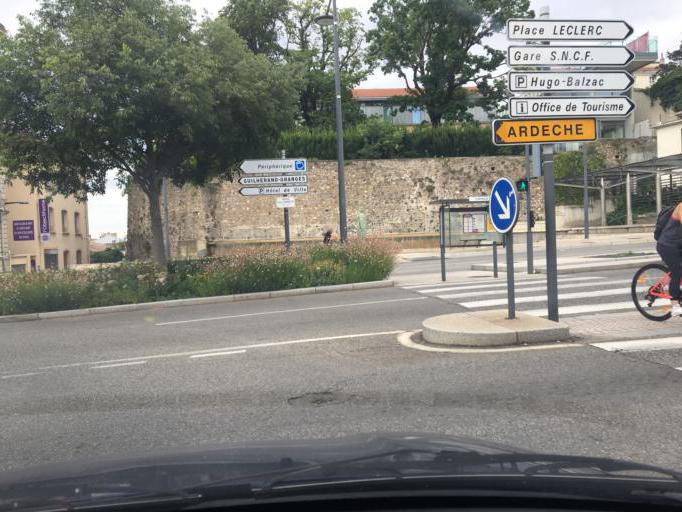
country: FR
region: Rhone-Alpes
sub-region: Departement de la Drome
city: Valence
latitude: 44.9305
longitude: 4.8885
